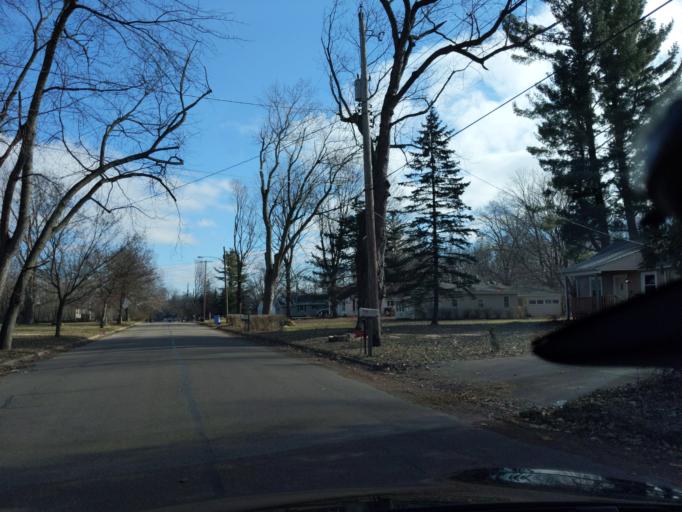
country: US
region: Michigan
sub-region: Ingham County
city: Lansing
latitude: 42.6819
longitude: -84.5868
